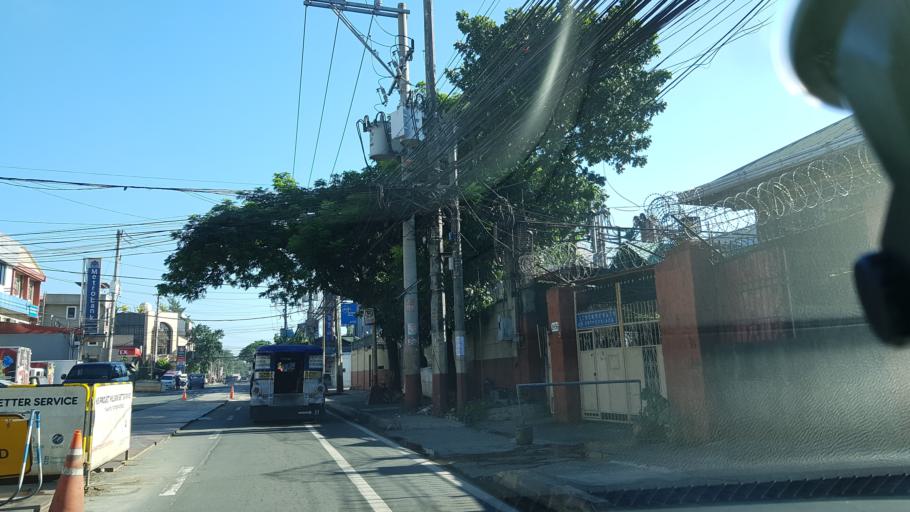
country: PH
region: Metro Manila
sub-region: Pasig
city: Pasig City
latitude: 14.5843
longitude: 121.0881
